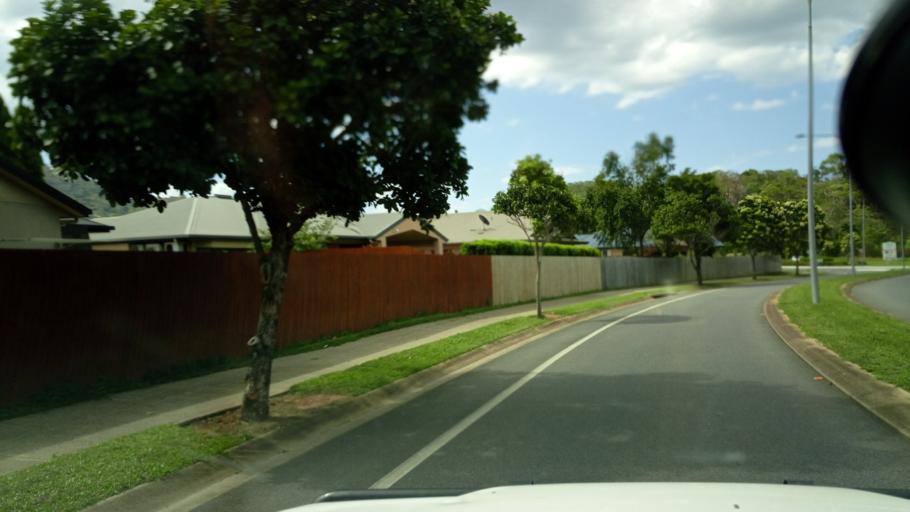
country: AU
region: Queensland
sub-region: Cairns
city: Woree
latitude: -16.9254
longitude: 145.7293
